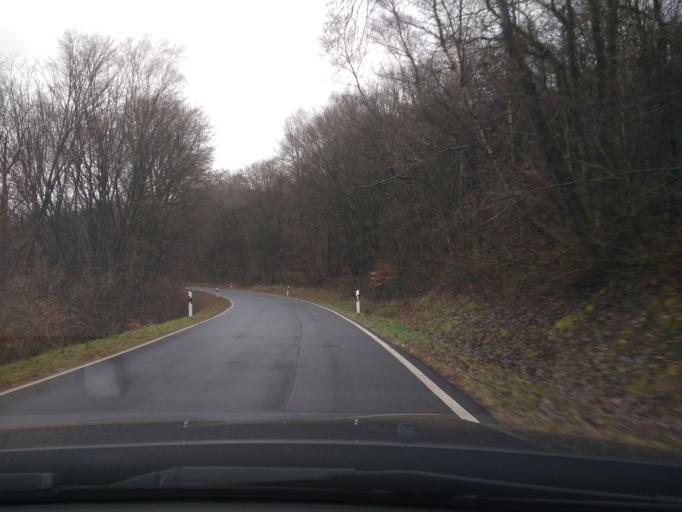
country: DE
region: Rheinland-Pfalz
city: Schomerich
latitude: 49.6388
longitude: 6.7088
